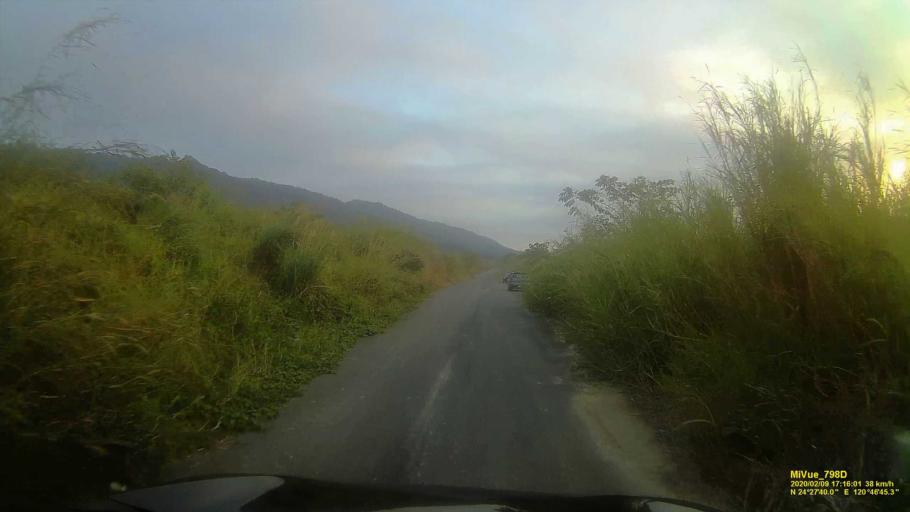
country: TW
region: Taiwan
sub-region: Miaoli
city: Miaoli
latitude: 24.4609
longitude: 120.7793
